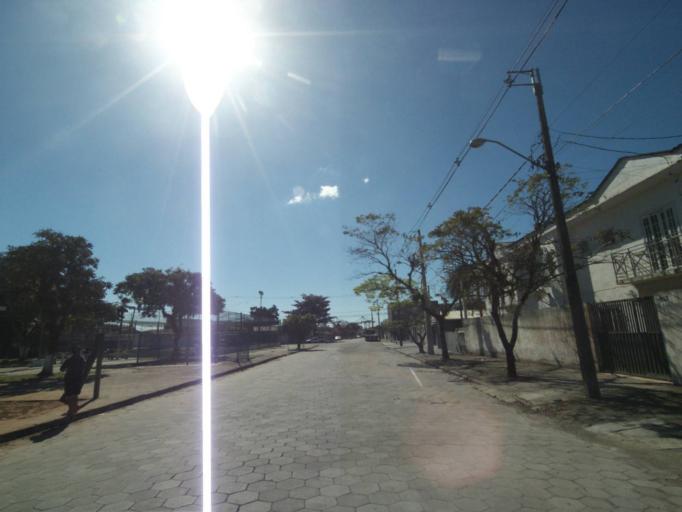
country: BR
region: Parana
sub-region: Paranagua
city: Paranagua
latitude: -25.5125
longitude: -48.5028
